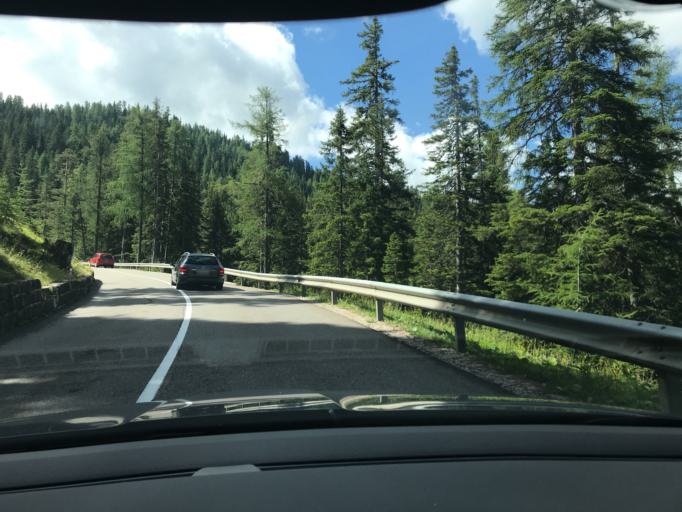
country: IT
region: Veneto
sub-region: Provincia di Belluno
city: Livinallongo del Col di Lana
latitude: 46.5511
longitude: 11.9773
